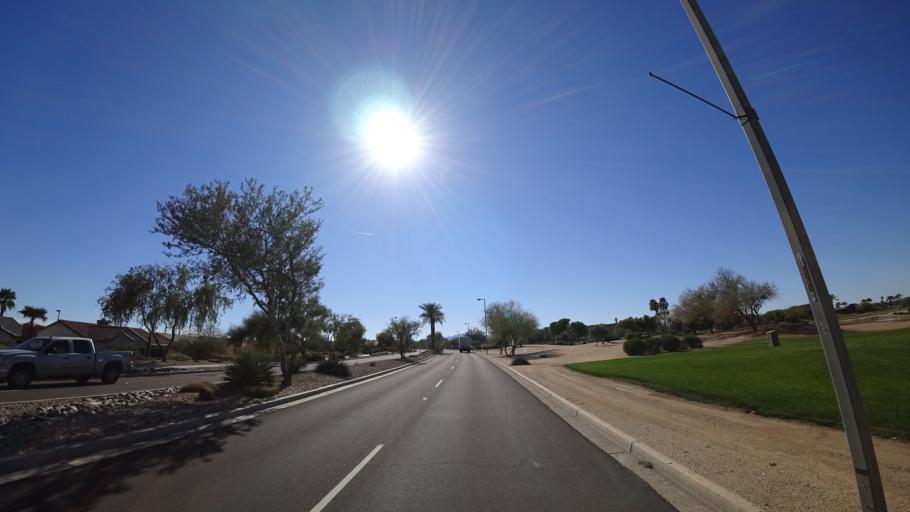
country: US
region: Arizona
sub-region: Maricopa County
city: Sun City West
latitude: 33.6616
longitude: -112.3995
